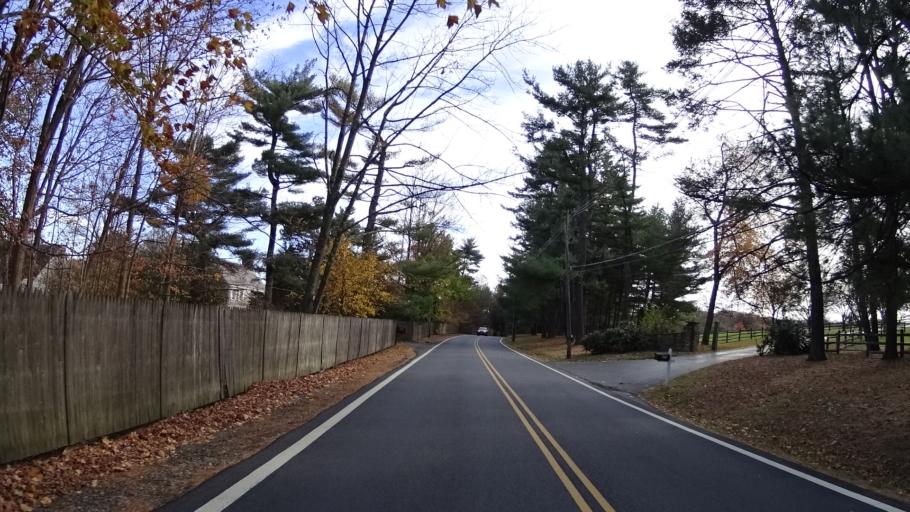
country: US
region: New Jersey
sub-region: Morris County
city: Morristown
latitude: 40.7647
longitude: -74.4578
